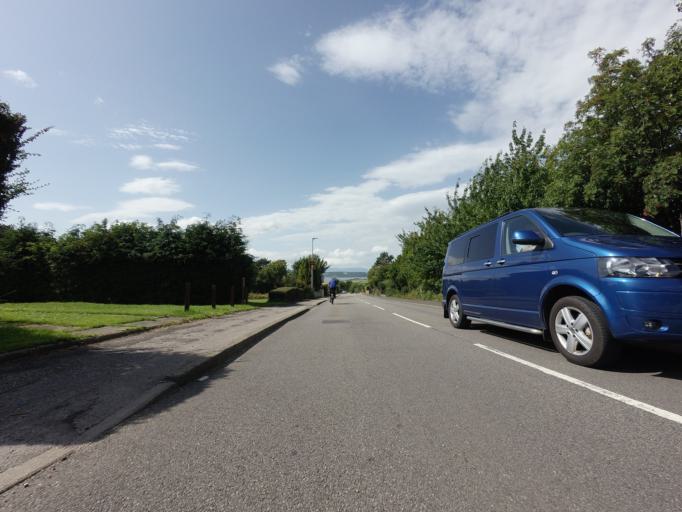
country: GB
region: Scotland
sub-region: Highland
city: Fortrose
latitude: 57.4935
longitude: -4.1118
